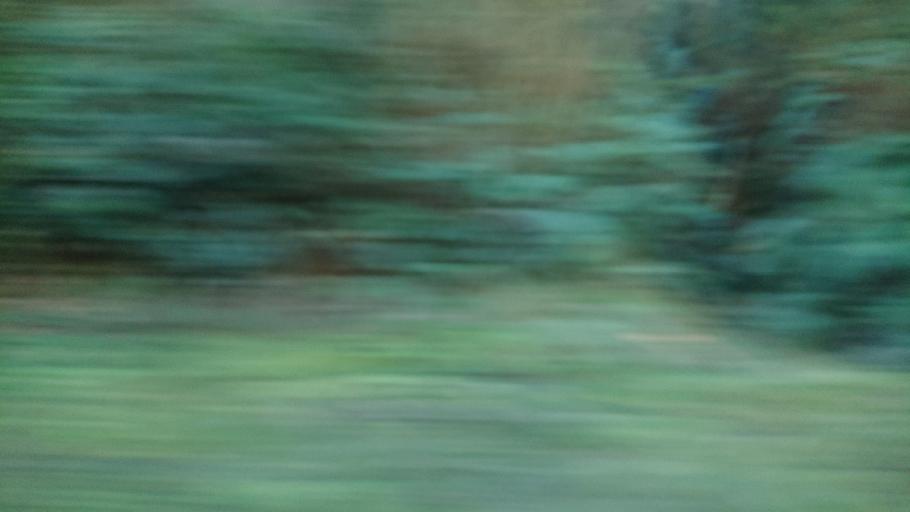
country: TW
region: Taiwan
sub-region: Hualien
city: Hualian
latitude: 24.3778
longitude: 121.3396
